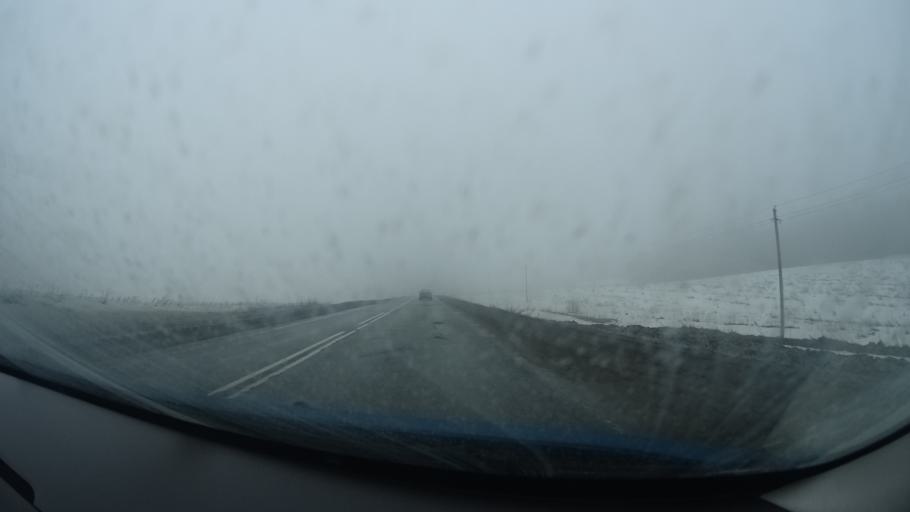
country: RU
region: Perm
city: Kuyeda
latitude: 56.4670
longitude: 55.6740
